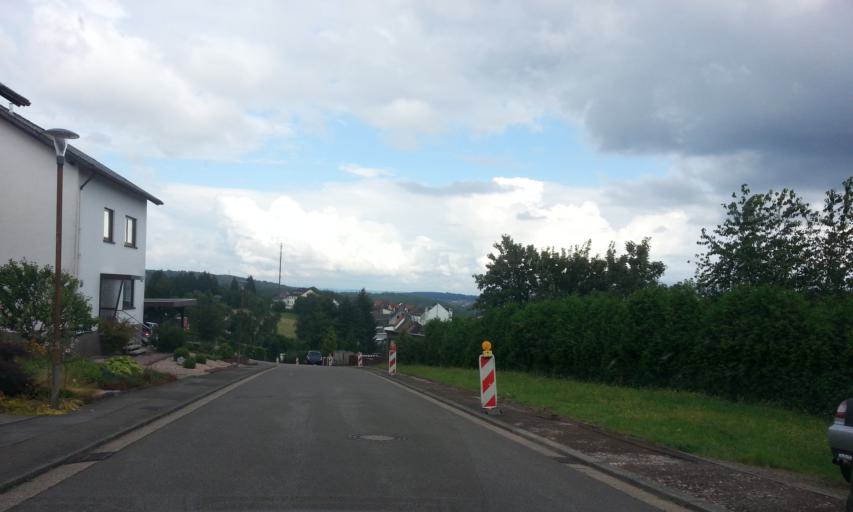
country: DE
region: Saarland
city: Schiffweiler
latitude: 49.3568
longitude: 7.1192
